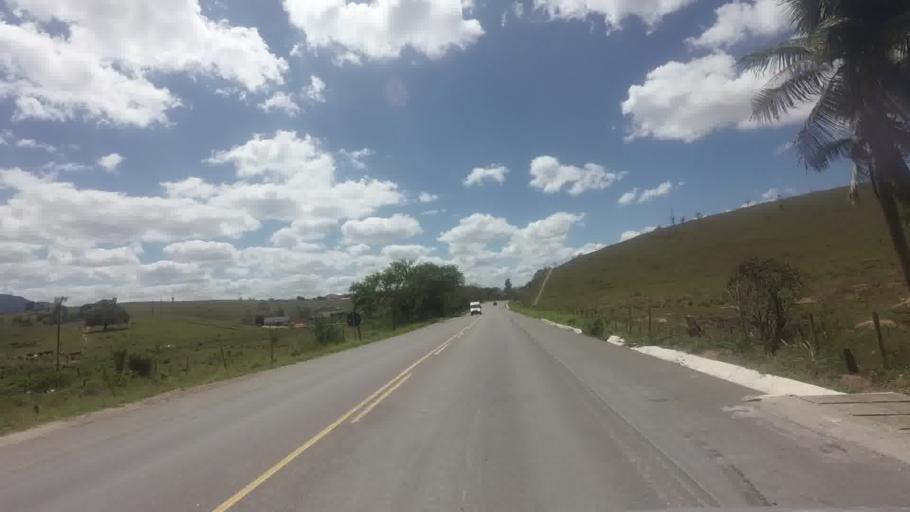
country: BR
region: Minas Gerais
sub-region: Recreio
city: Recreio
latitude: -21.6557
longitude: -42.3675
